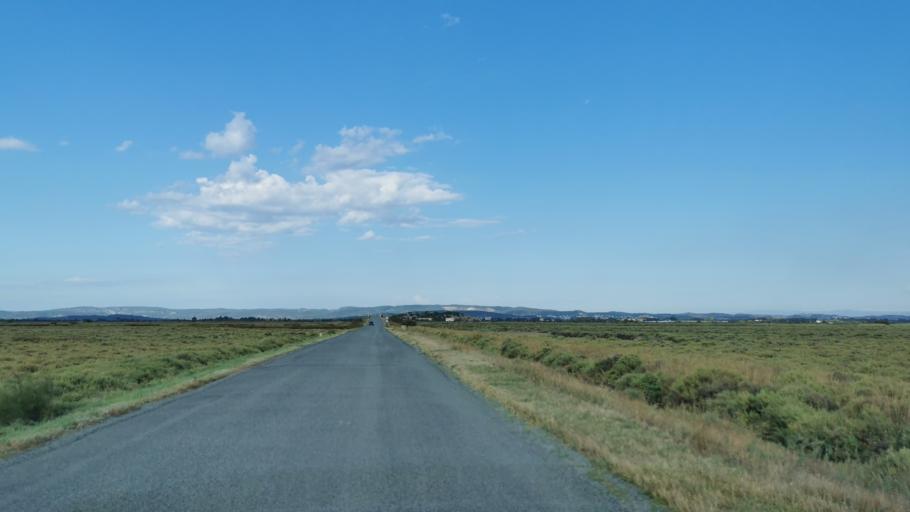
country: FR
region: Languedoc-Roussillon
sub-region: Departement de l'Aude
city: Gruissan
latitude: 43.1100
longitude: 3.0620
